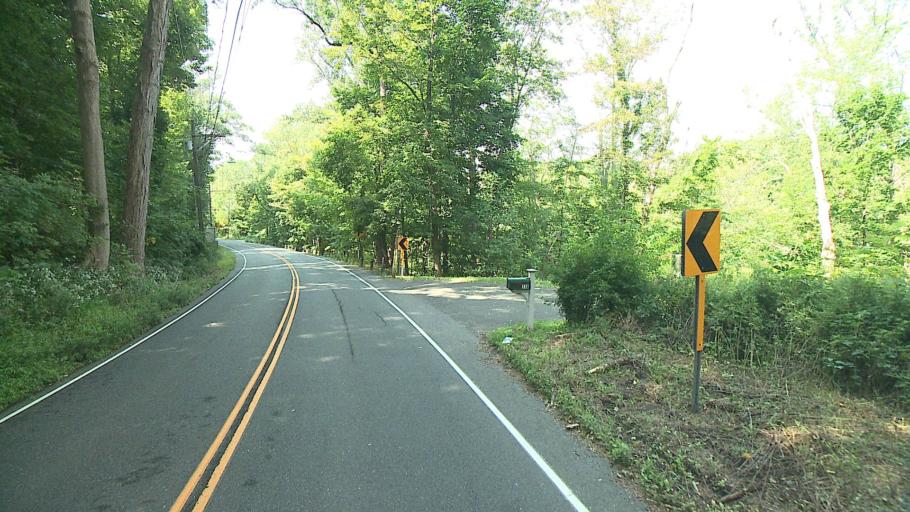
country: US
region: Connecticut
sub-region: Fairfield County
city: Ridgefield
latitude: 41.2679
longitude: -73.5158
